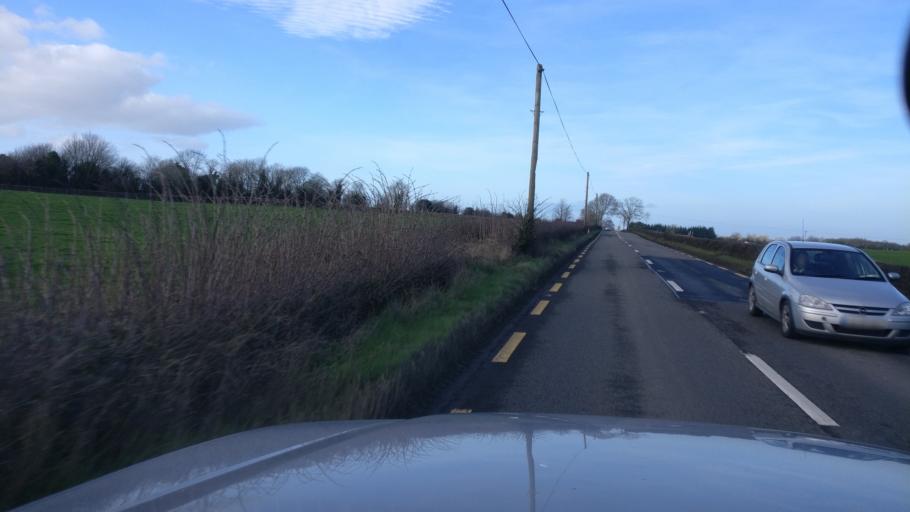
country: IE
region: Leinster
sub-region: Laois
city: Mountmellick
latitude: 53.0958
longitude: -7.3372
